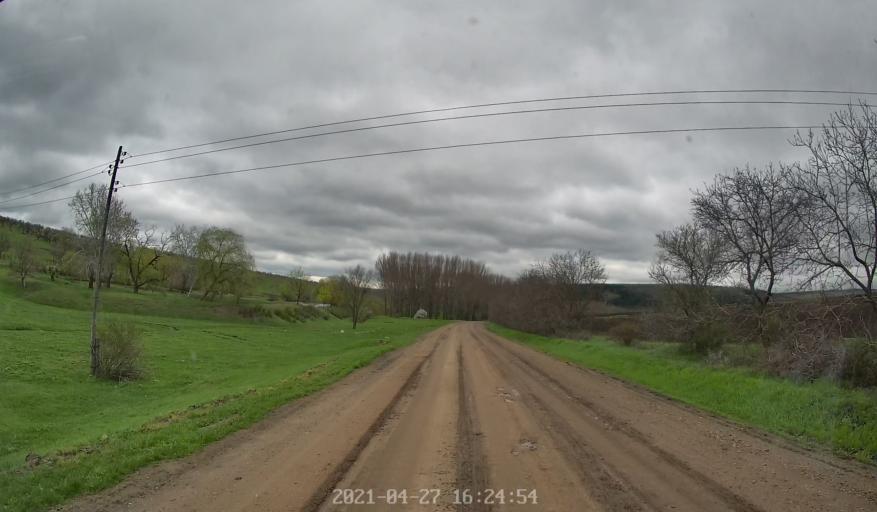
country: MD
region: Chisinau
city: Singera
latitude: 46.9886
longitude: 29.0215
